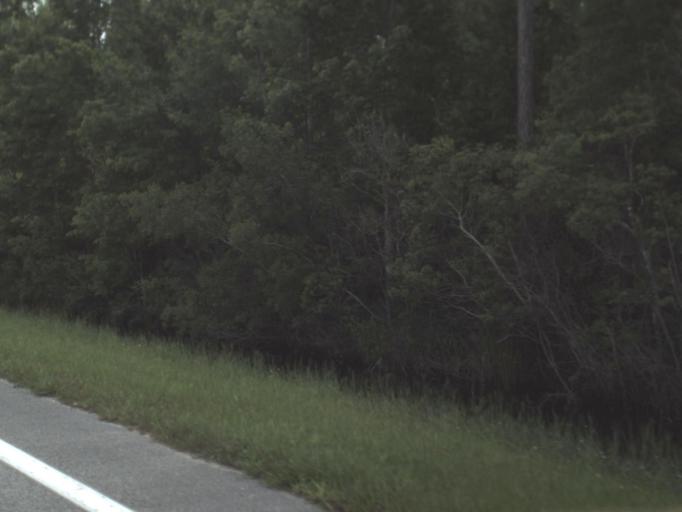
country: US
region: Florida
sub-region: Levy County
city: Bronson
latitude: 29.3928
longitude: -82.7004
